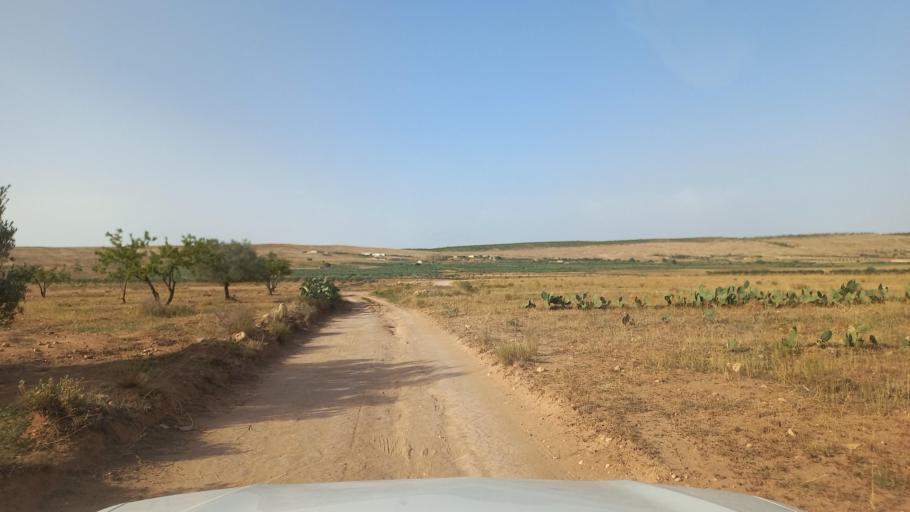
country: TN
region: Al Qasrayn
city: Kasserine
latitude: 35.3515
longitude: 8.8484
